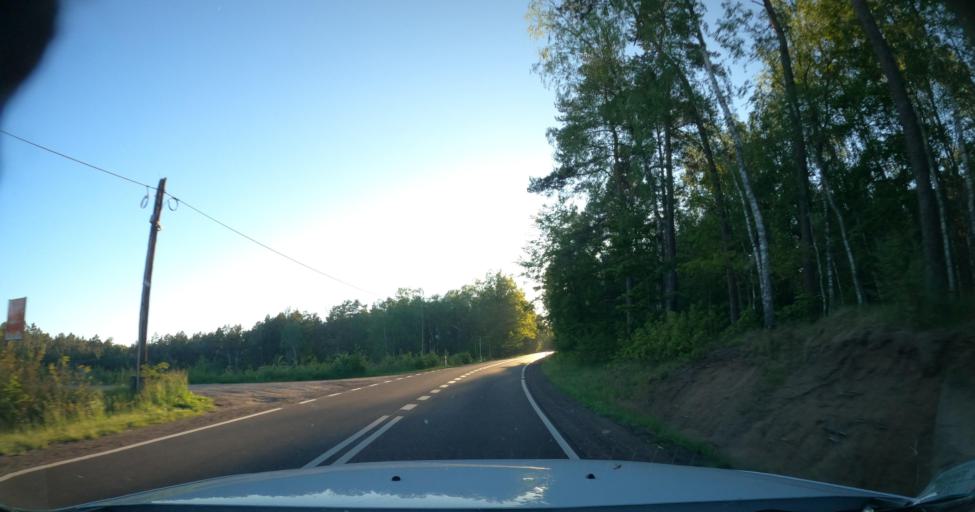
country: PL
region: Pomeranian Voivodeship
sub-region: Powiat bytowski
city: Czarna Dabrowka
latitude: 54.3405
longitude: 17.6128
